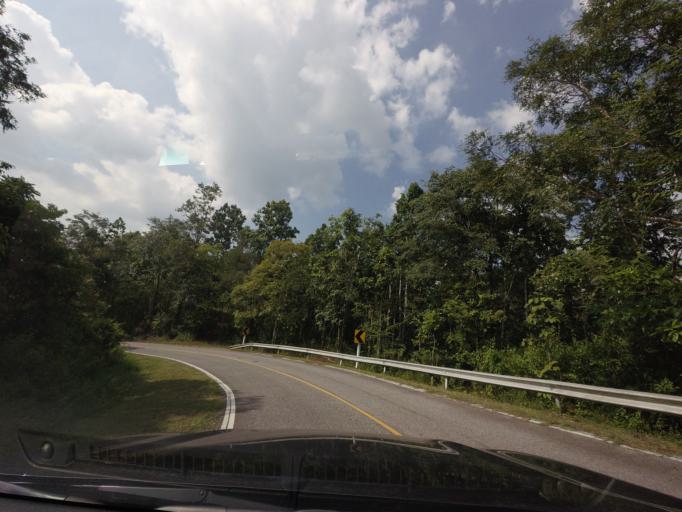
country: TH
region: Uttaradit
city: Ban Khok
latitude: 18.1701
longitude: 101.0799
